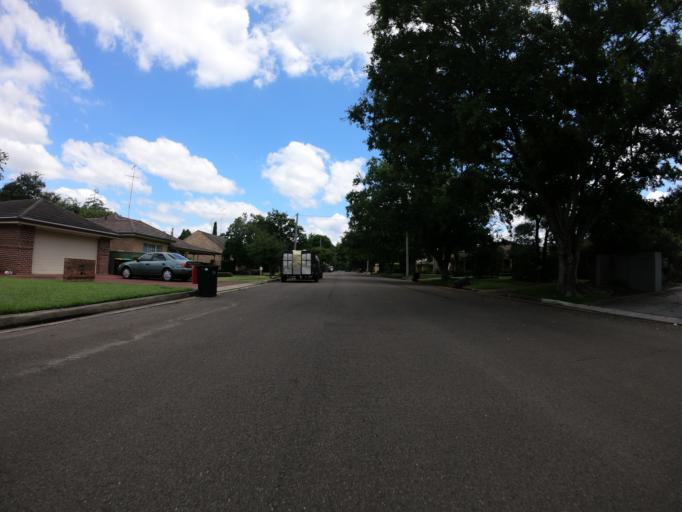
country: AU
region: New South Wales
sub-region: Penrith Municipality
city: Penrith
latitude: -33.7513
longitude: 150.6789
